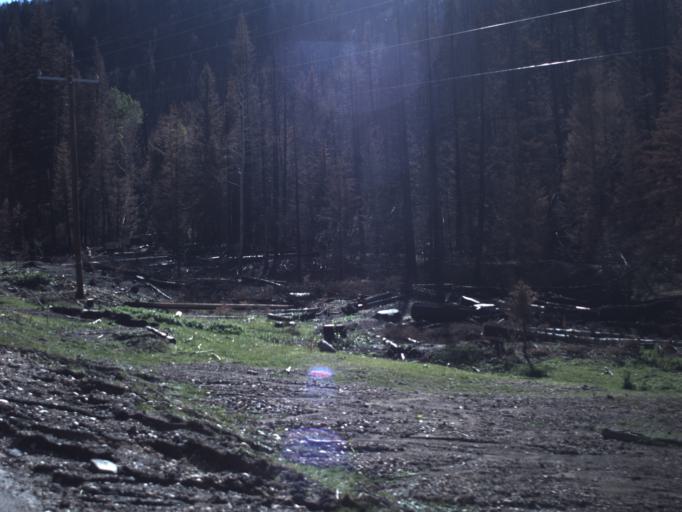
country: US
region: Utah
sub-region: Iron County
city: Parowan
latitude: 37.7414
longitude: -112.8378
